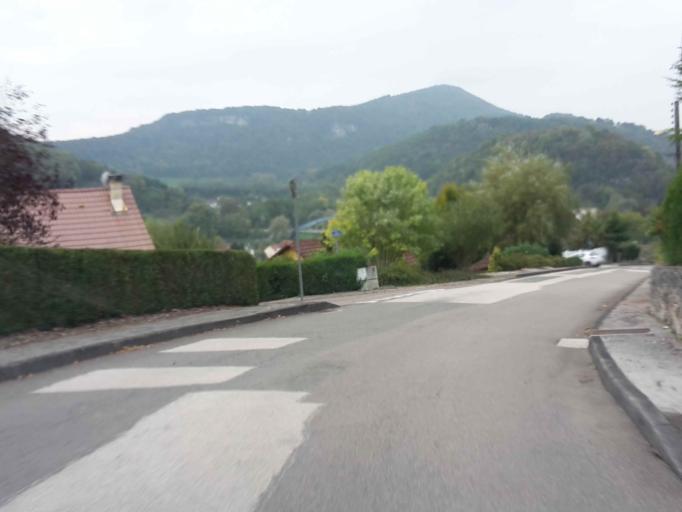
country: FR
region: Franche-Comte
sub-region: Departement du Doubs
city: Baume-les-Dames
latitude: 47.3466
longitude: 6.3682
